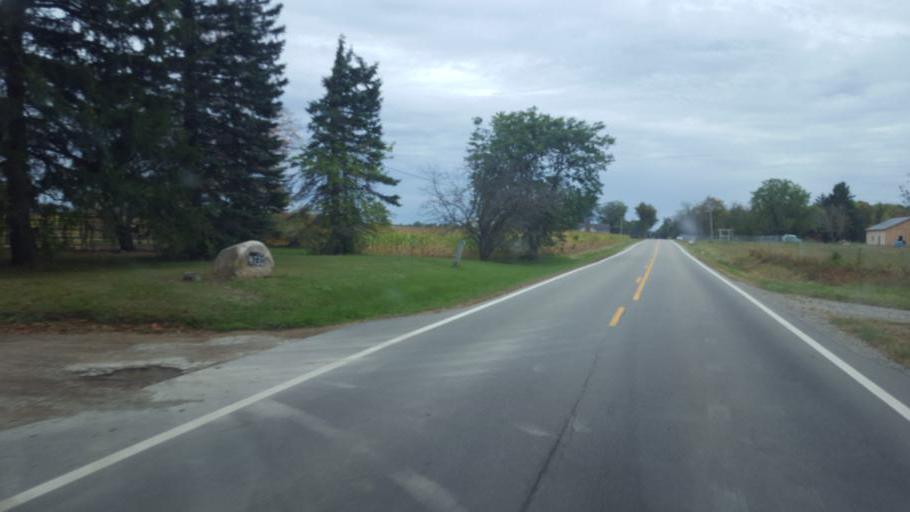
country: US
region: Ohio
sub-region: Huron County
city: Wakeman
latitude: 41.2656
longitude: -82.3961
